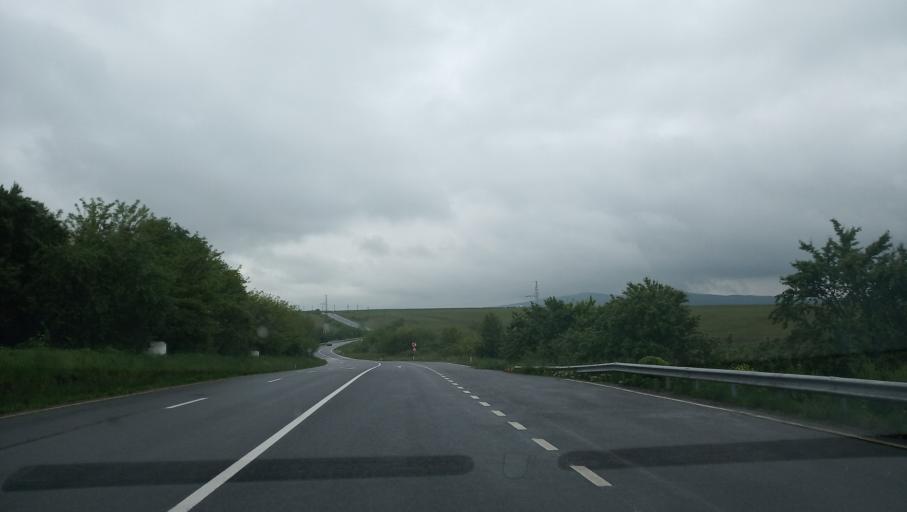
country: RO
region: Alba
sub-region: Comuna Cut
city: Cut
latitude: 45.9193
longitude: 23.6983
